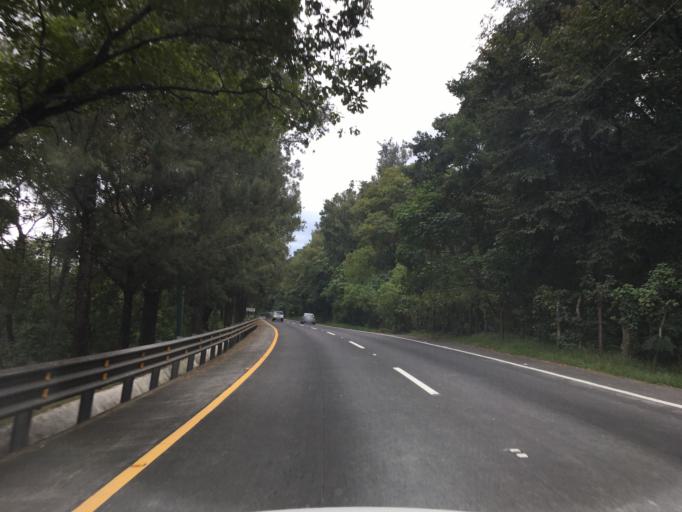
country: GT
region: Sacatepequez
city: Santa Lucia Milpas Altas
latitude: 14.5674
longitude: -90.6836
